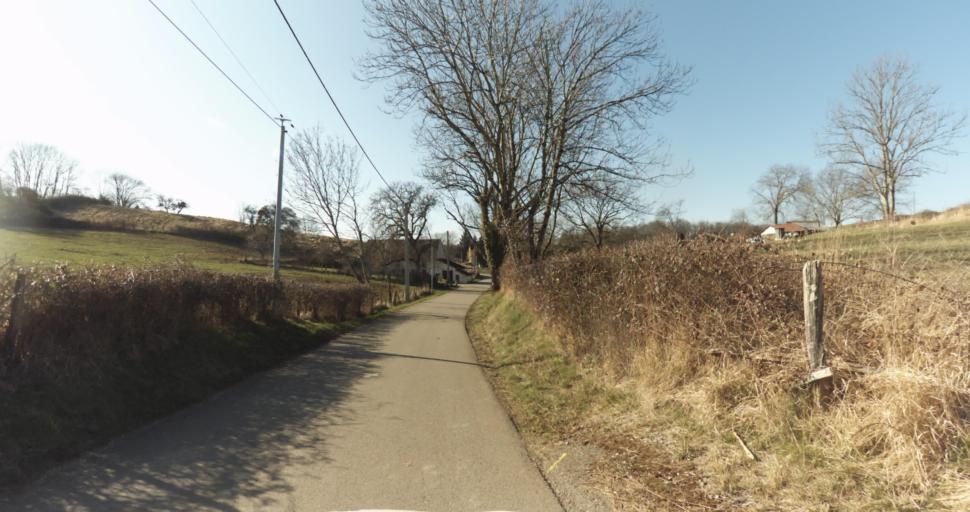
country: FR
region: Franche-Comte
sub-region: Departement du Jura
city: Montmorot
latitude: 46.6960
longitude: 5.5205
